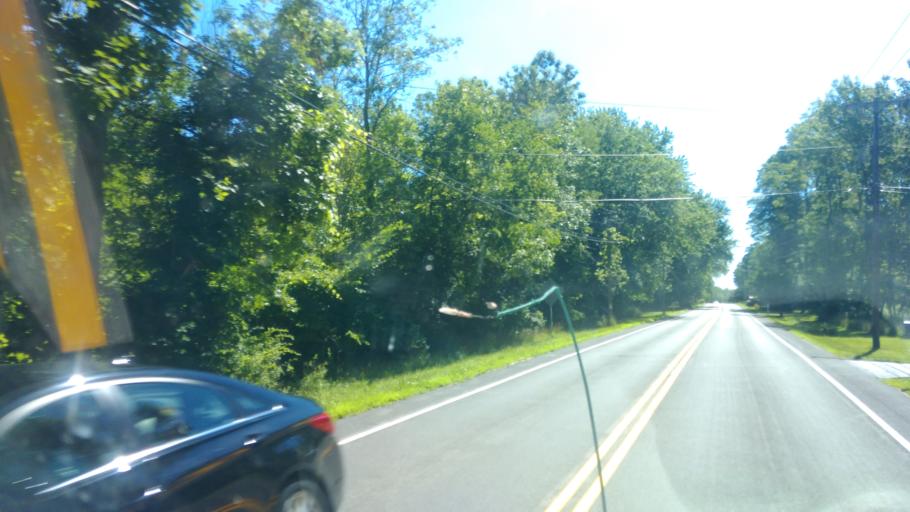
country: US
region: New York
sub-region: Monroe County
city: Webster
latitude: 43.2693
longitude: -77.3868
